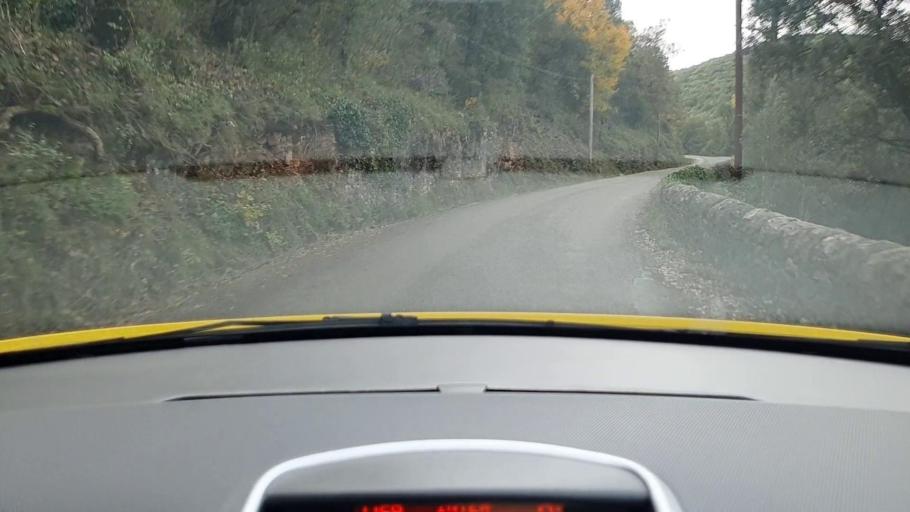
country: FR
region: Languedoc-Roussillon
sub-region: Departement du Gard
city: Anduze
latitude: 44.0543
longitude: 3.9235
